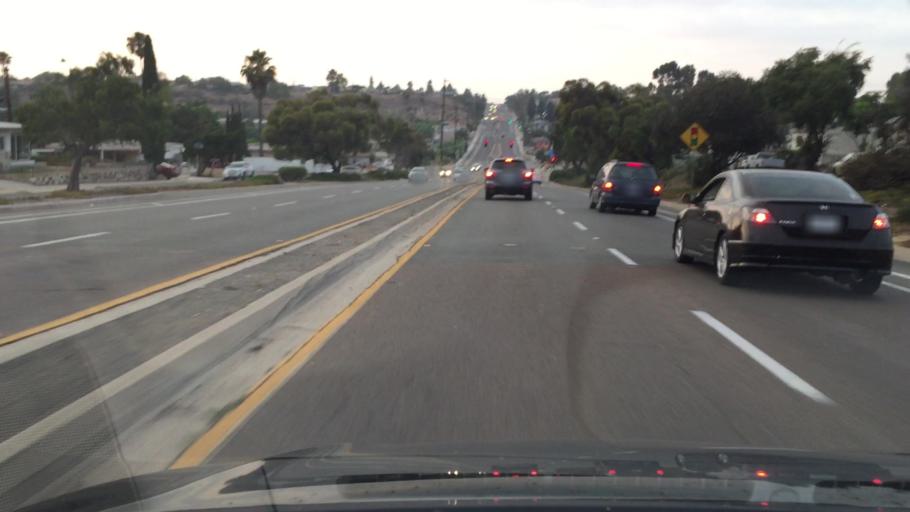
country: US
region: California
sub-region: San Diego County
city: Lemon Grove
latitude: 32.7412
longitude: -117.0796
